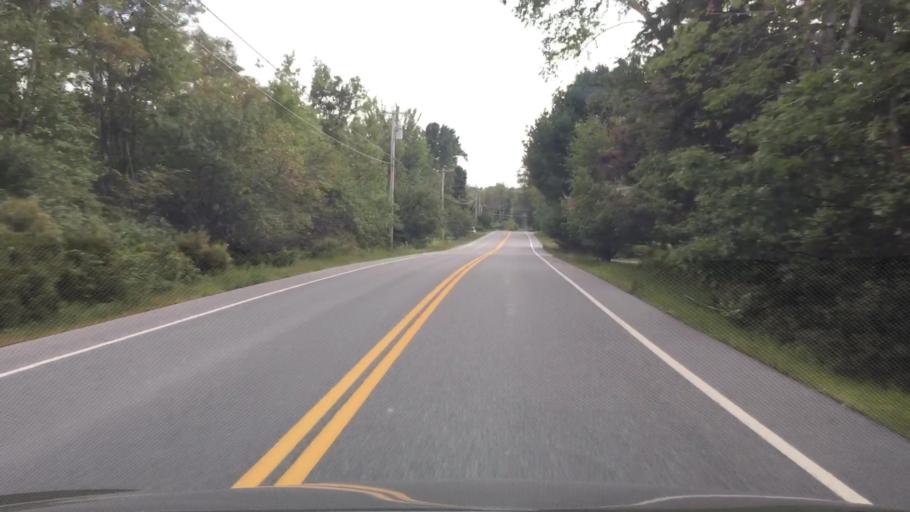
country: US
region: Maine
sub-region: Hancock County
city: Castine
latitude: 44.4364
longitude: -68.7927
